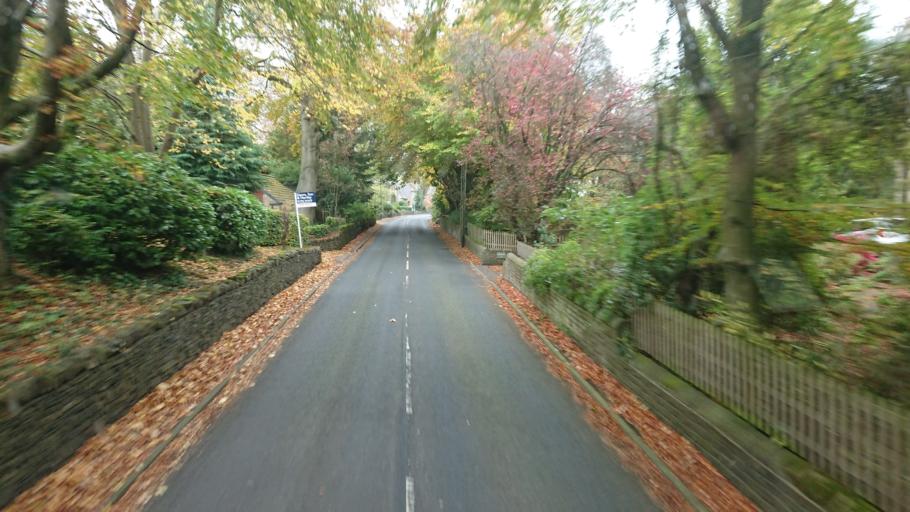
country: GB
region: England
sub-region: North Yorkshire
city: Skipton
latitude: 53.9655
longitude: -2.0216
